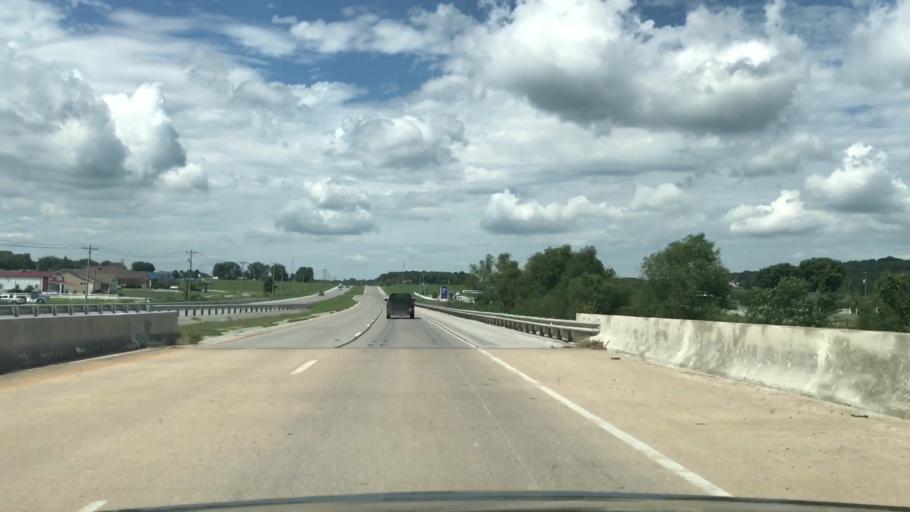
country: US
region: Kentucky
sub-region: Logan County
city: Russellville
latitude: 36.8665
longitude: -86.8791
